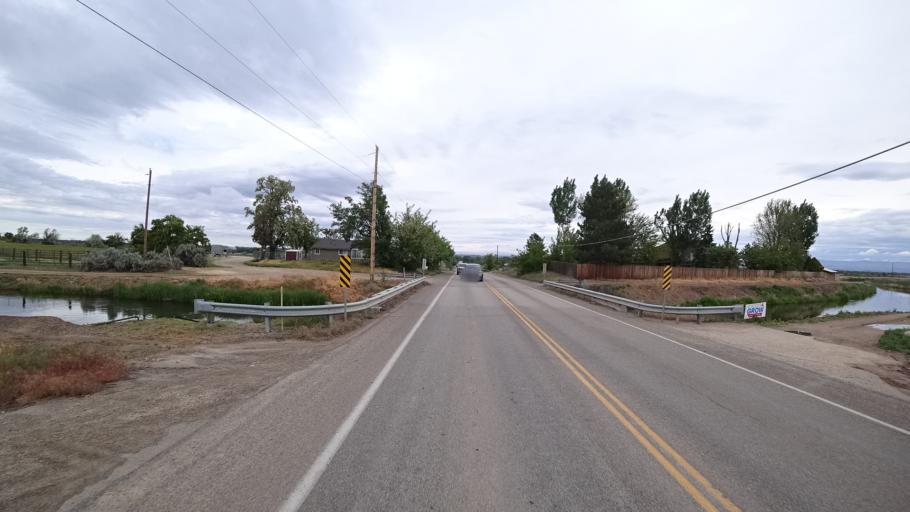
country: US
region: Idaho
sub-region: Ada County
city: Star
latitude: 43.6664
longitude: -116.4934
